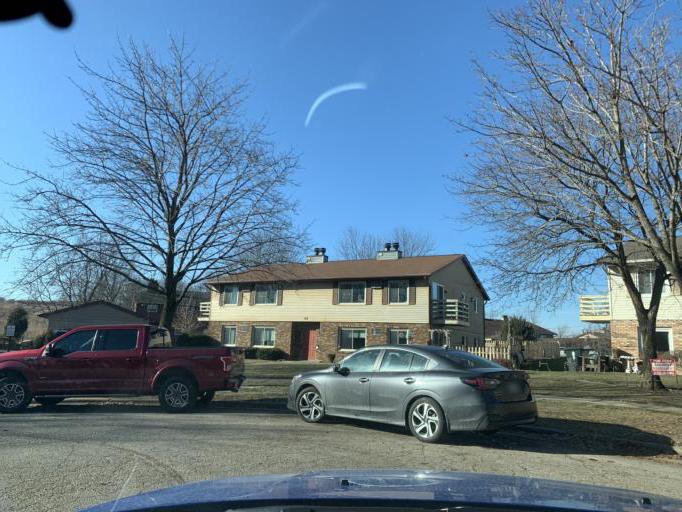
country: US
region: Wisconsin
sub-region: Dane County
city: Verona
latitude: 43.0371
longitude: -89.4967
